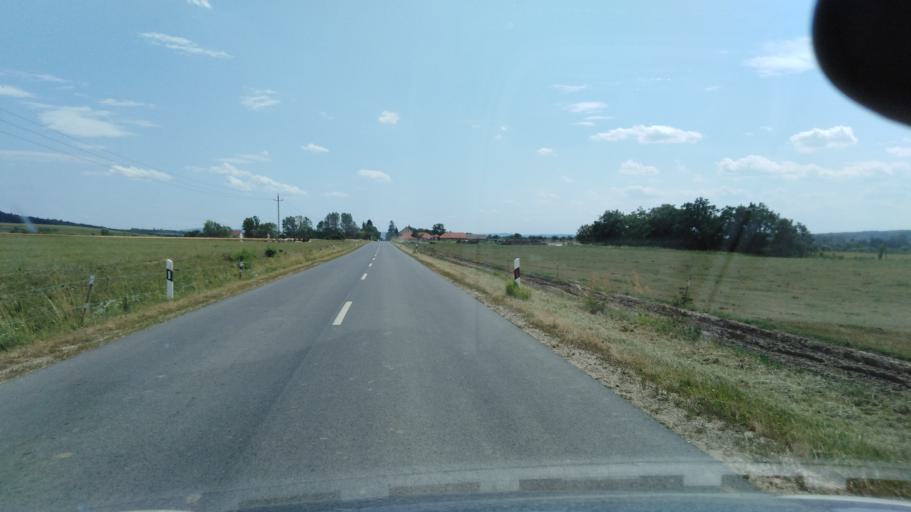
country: HU
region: Nograd
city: Szecseny
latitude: 48.1561
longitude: 19.5338
